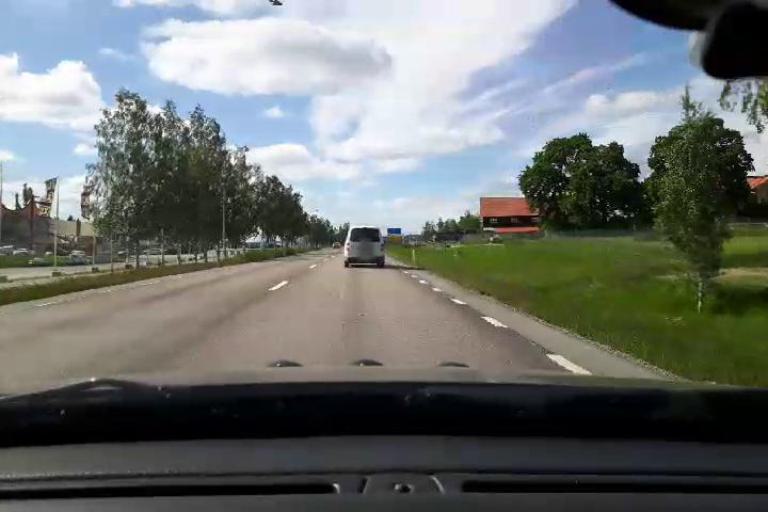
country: SE
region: Gaevleborg
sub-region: Bollnas Kommun
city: Bollnas
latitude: 61.3350
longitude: 16.4025
